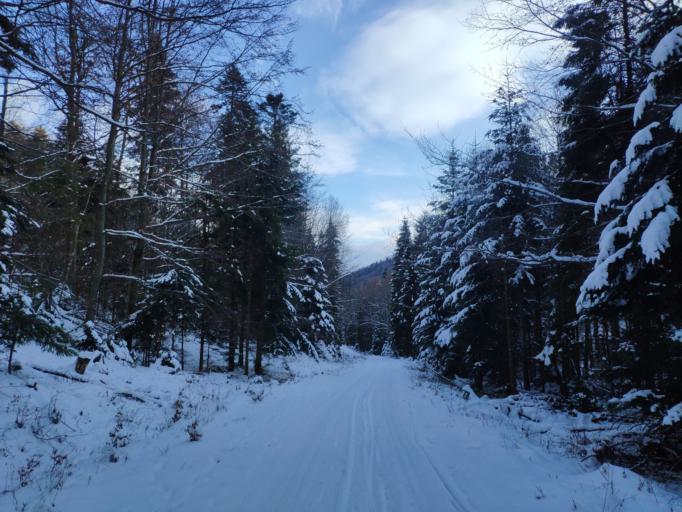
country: SK
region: Kosicky
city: Gelnica
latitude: 48.7654
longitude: 20.9626
